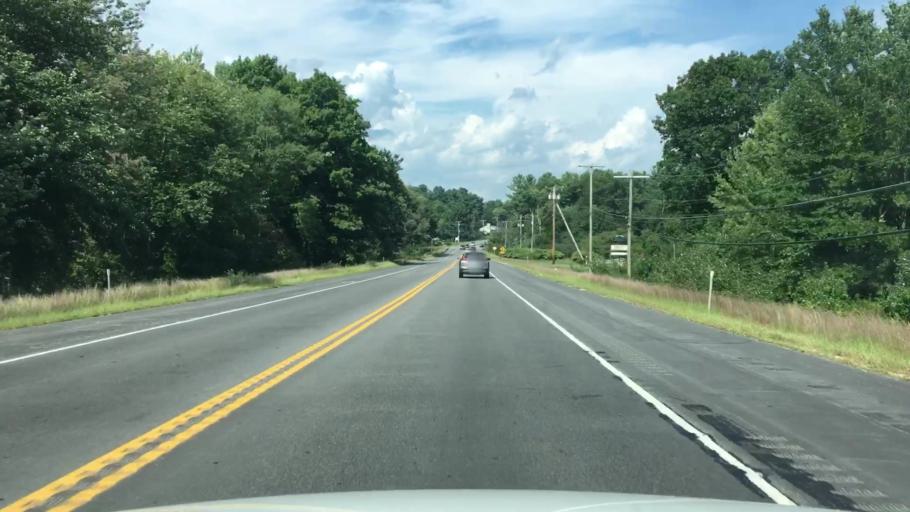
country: US
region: New Hampshire
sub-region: Rockingham County
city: Londonderry
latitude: 42.8536
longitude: -71.3568
